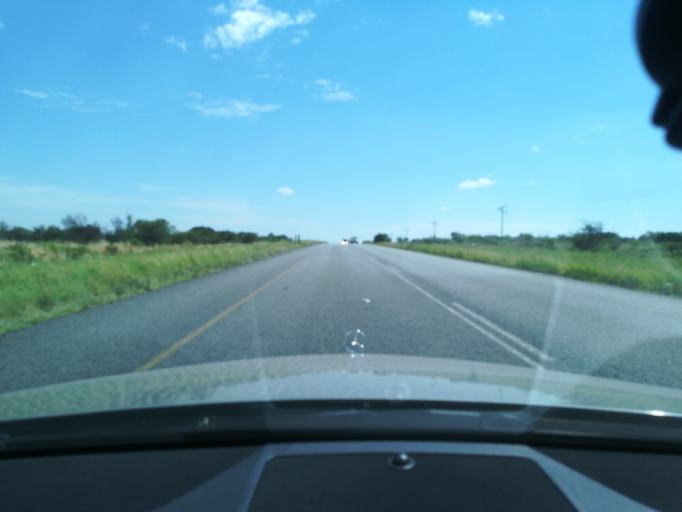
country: ZA
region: North-West
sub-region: Dr Kenneth Kaunda District Municipality
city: Wolmaransstad
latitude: -27.0135
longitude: 26.1777
